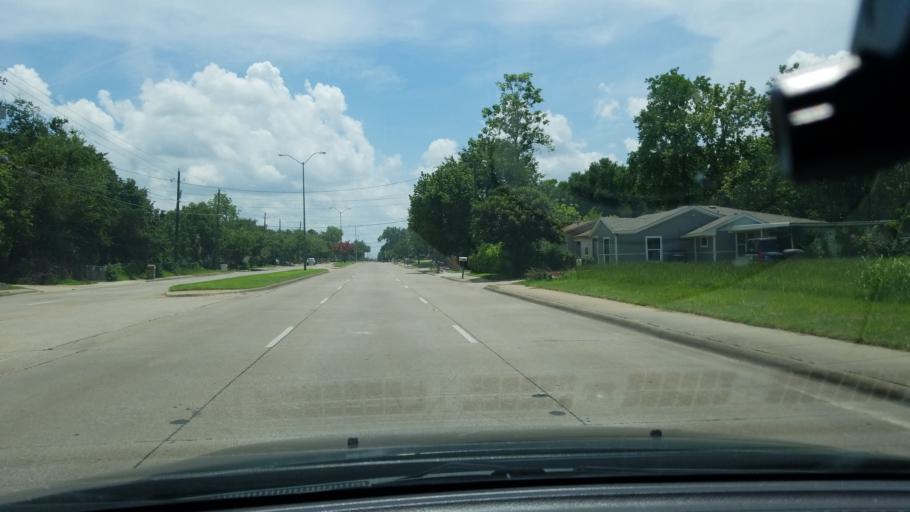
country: US
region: Texas
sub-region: Dallas County
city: Balch Springs
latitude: 32.7179
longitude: -96.6485
